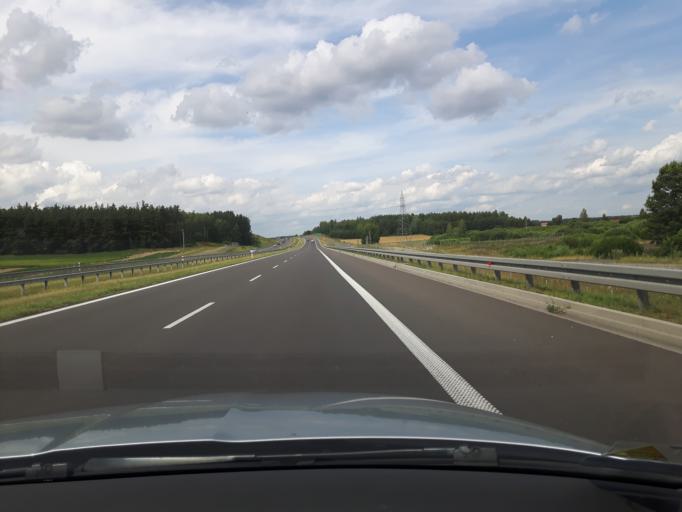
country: PL
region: Warmian-Masurian Voivodeship
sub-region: Powiat nidzicki
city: Nidzica
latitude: 53.3607
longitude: 20.3902
